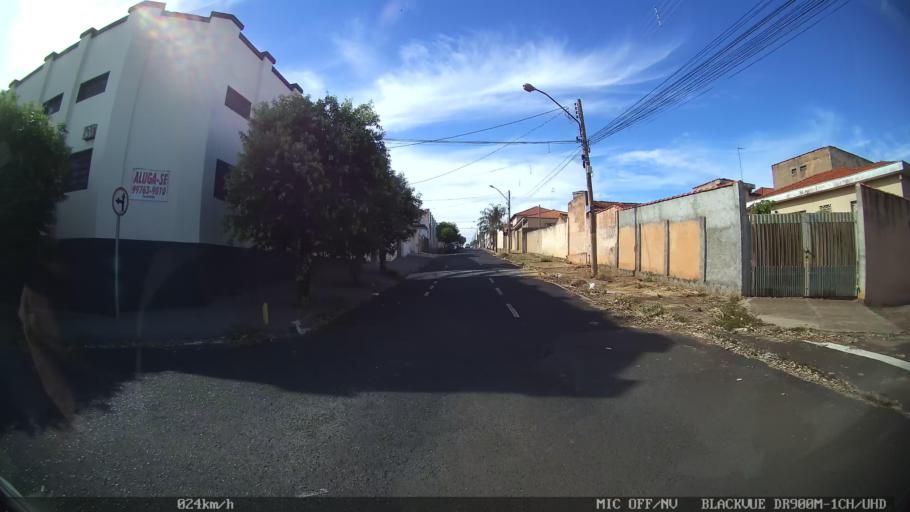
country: BR
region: Sao Paulo
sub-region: Catanduva
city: Catanduva
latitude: -21.1322
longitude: -48.9654
